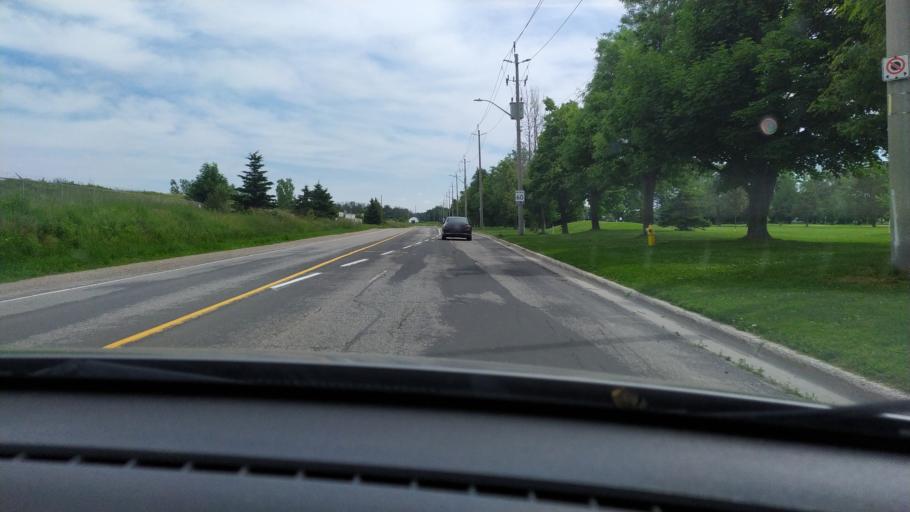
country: CA
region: Ontario
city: Stratford
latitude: 43.3567
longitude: -80.9632
